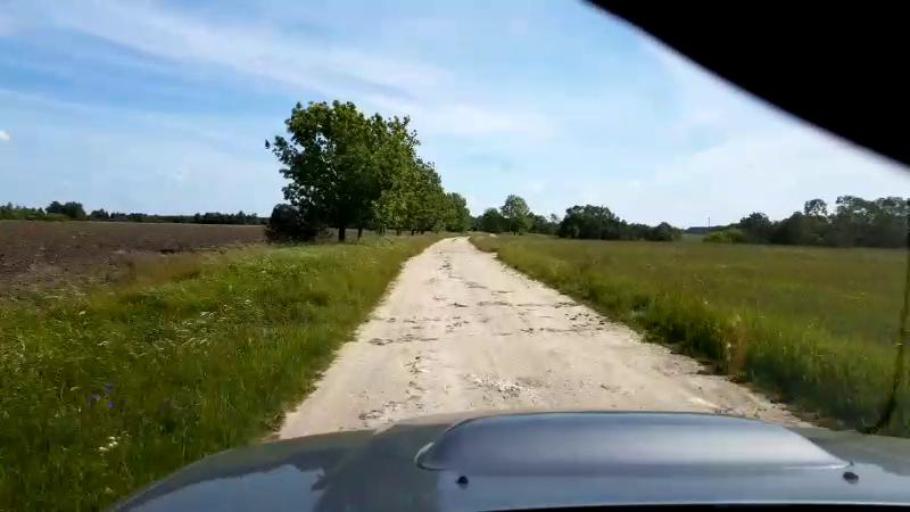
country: EE
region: Paernumaa
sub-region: Sauga vald
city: Sauga
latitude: 58.4939
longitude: 24.5343
